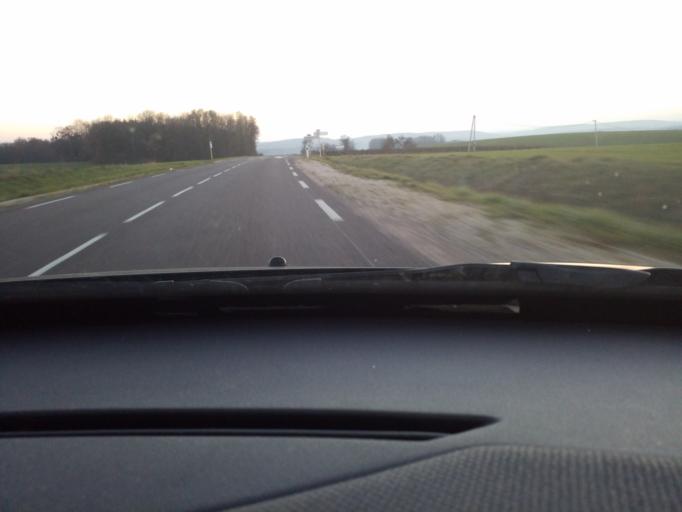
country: FR
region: Franche-Comte
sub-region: Departement de la Haute-Saone
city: Faverney
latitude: 47.9000
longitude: 6.0760
